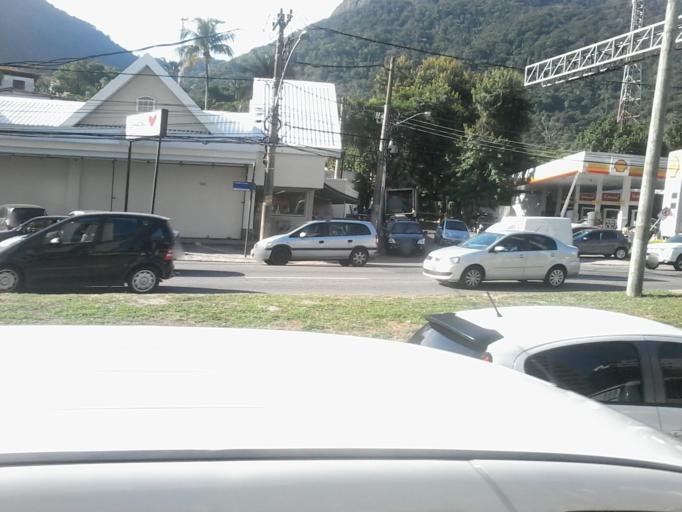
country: BR
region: Rio de Janeiro
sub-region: Rio De Janeiro
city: Rio de Janeiro
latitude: -22.9988
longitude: -43.2679
